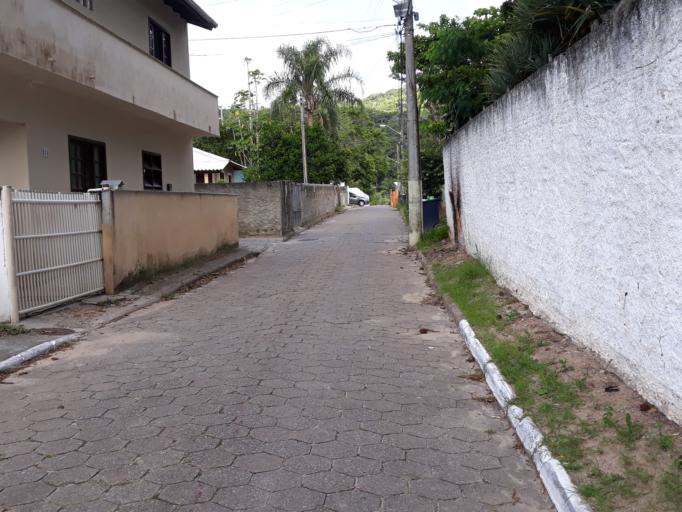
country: BR
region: Santa Catarina
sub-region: Florianopolis
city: Itacorubi
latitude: -27.4242
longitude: -48.4242
